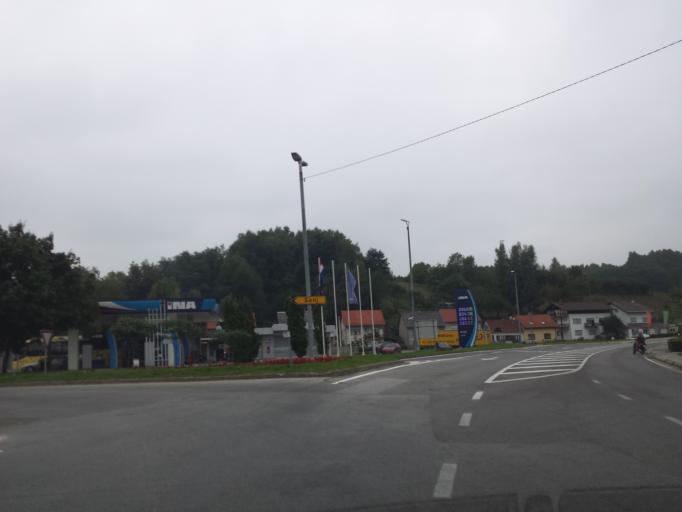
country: HR
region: Karlovacka
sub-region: Grad Karlovac
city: Karlovac
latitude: 45.4578
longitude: 15.4911
